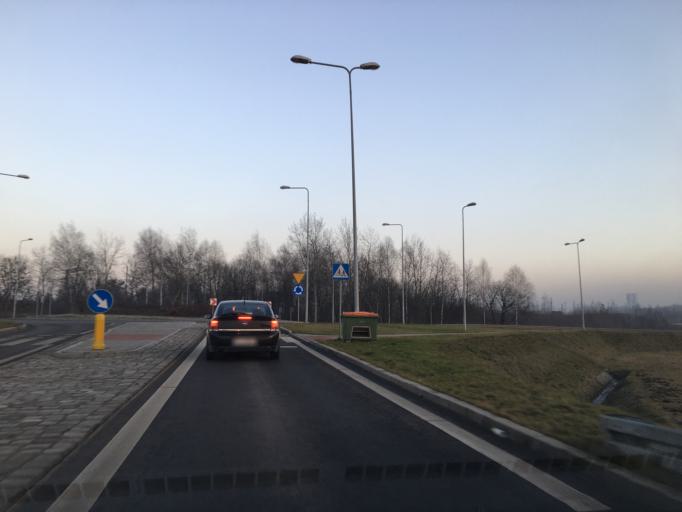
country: PL
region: Silesian Voivodeship
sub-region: Powiat tarnogorski
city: Radzionkow
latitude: 50.3660
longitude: 18.8758
